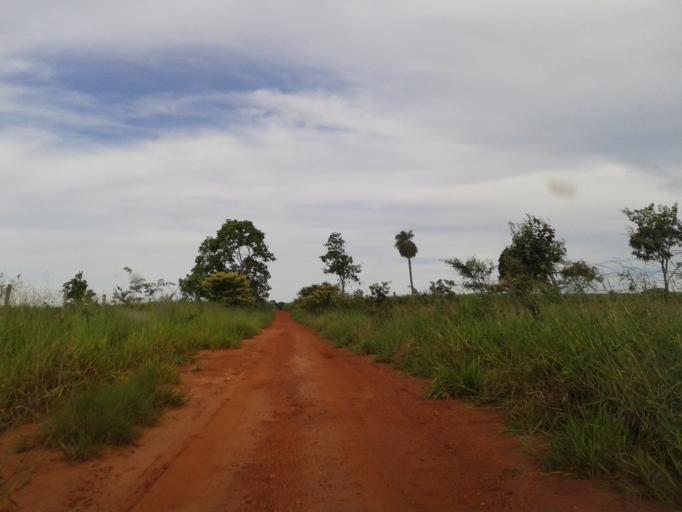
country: BR
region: Minas Gerais
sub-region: Capinopolis
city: Capinopolis
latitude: -18.7945
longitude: -49.8295
